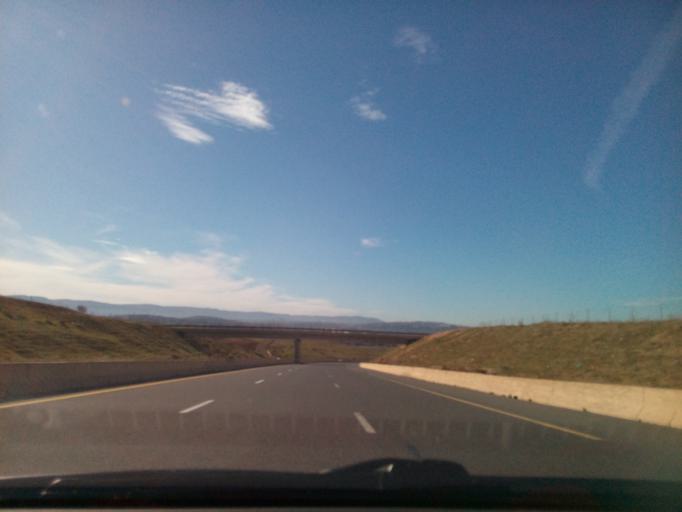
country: DZ
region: Tlemcen
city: Chetouane
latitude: 34.9631
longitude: -1.2714
